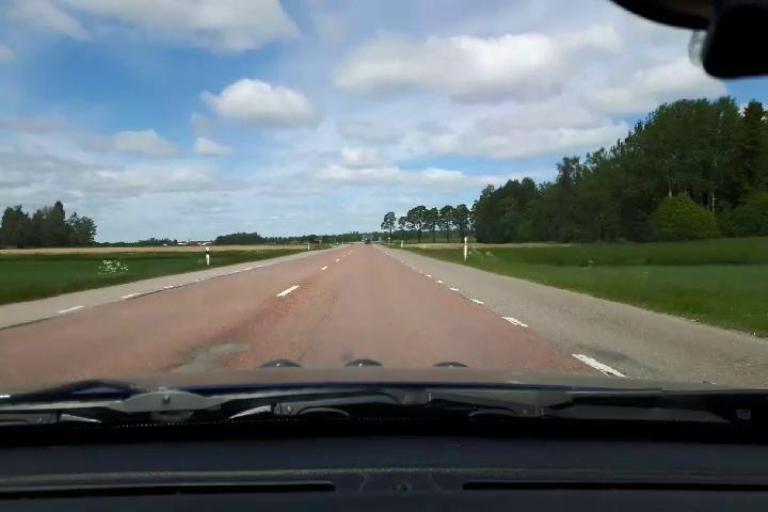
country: SE
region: Uppsala
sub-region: Osthammars Kommun
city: Bjorklinge
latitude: 60.0108
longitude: 17.5599
